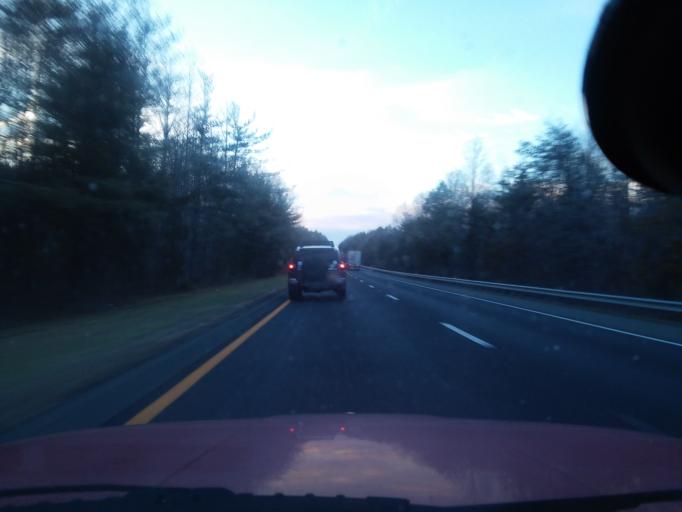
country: US
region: Virginia
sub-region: Fluvanna County
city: Palmyra
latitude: 37.9626
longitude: -78.1770
